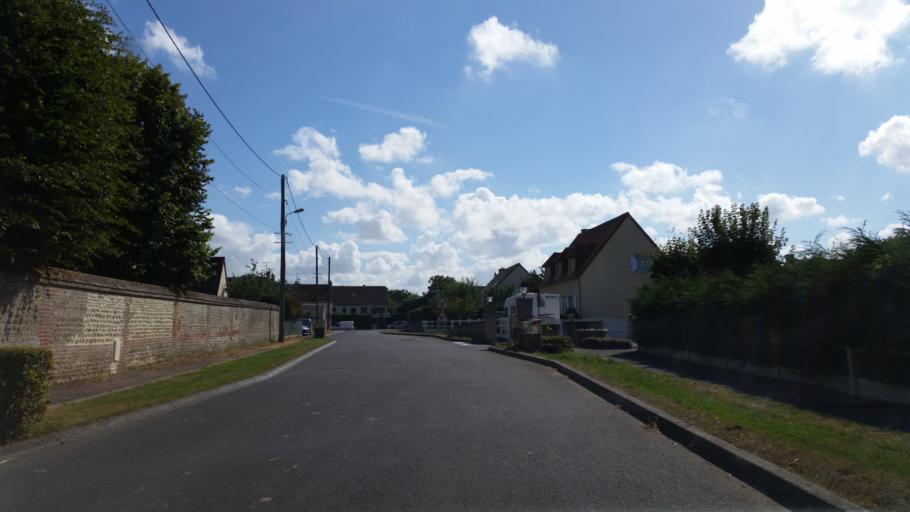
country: FR
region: Lower Normandy
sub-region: Departement du Calvados
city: Amfreville
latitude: 49.2513
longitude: -0.2314
